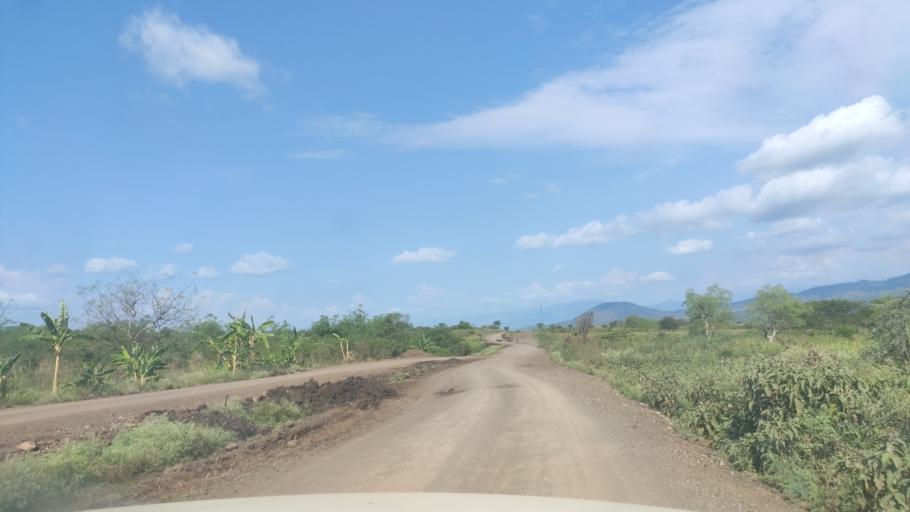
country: ET
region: Southern Nations, Nationalities, and People's Region
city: Felege Neway
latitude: 6.3945
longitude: 37.1023
